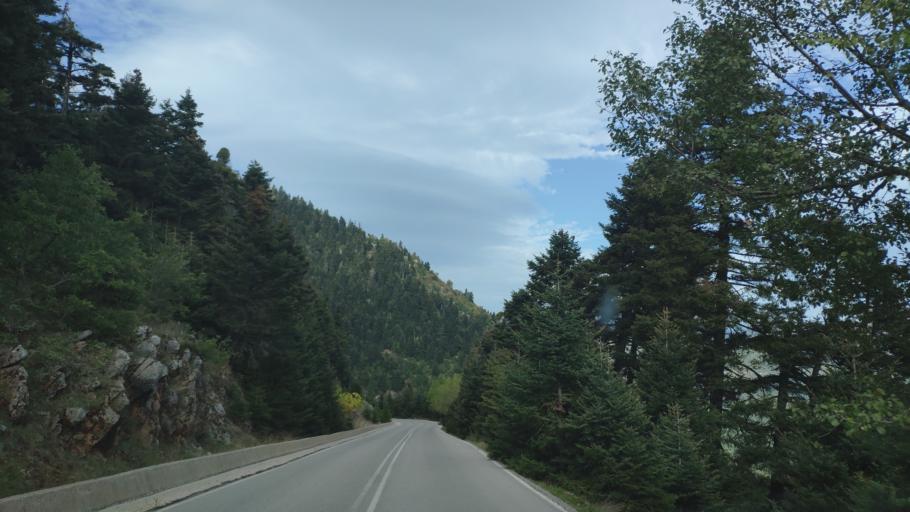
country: GR
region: Central Greece
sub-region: Nomos Fokidos
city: Amfissa
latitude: 38.6620
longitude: 22.3807
